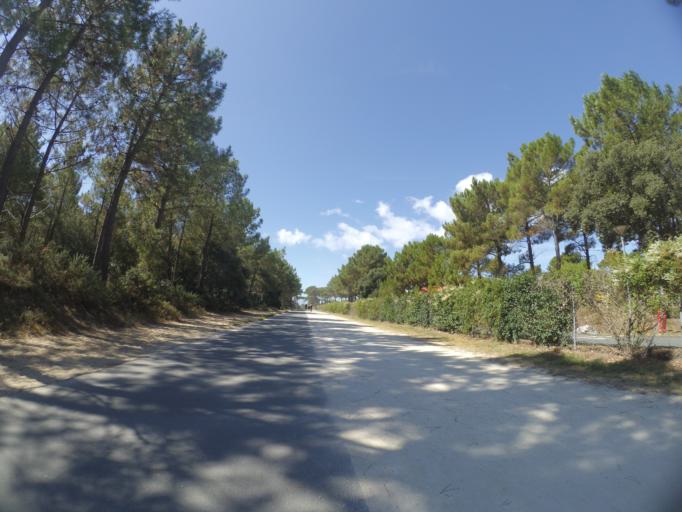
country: FR
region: Poitou-Charentes
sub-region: Departement de la Charente-Maritime
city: Les Mathes
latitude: 45.6788
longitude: -1.1600
